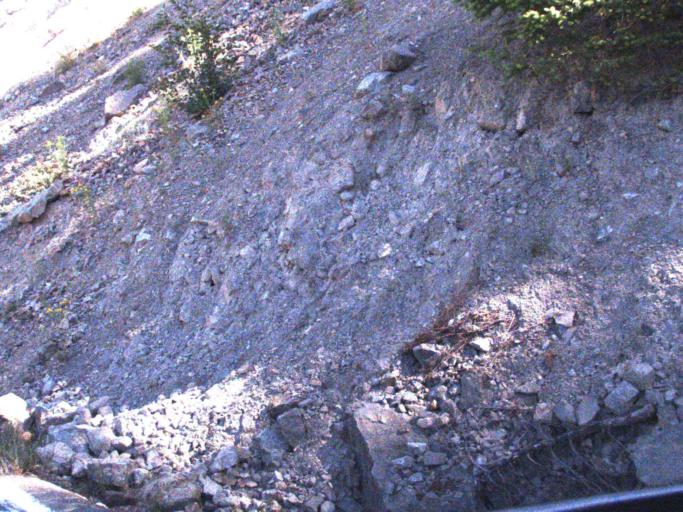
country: US
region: Washington
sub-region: King County
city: Enumclaw
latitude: 46.8848
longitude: -121.5410
